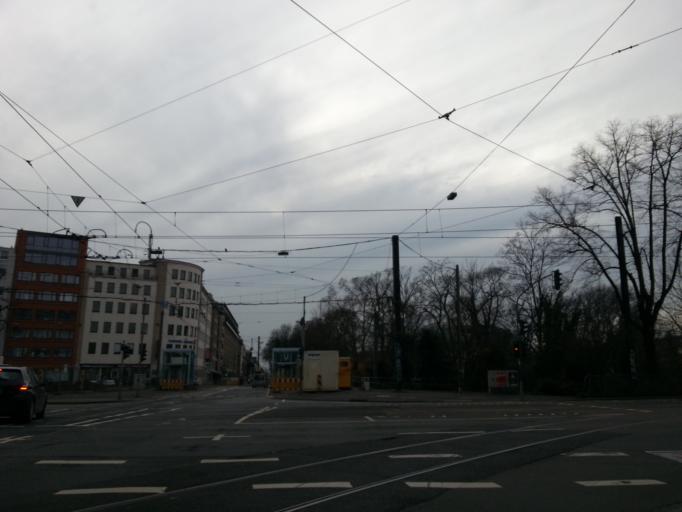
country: DE
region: North Rhine-Westphalia
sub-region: Regierungsbezirk Dusseldorf
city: Dusseldorf
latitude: 51.2191
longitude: 6.7757
